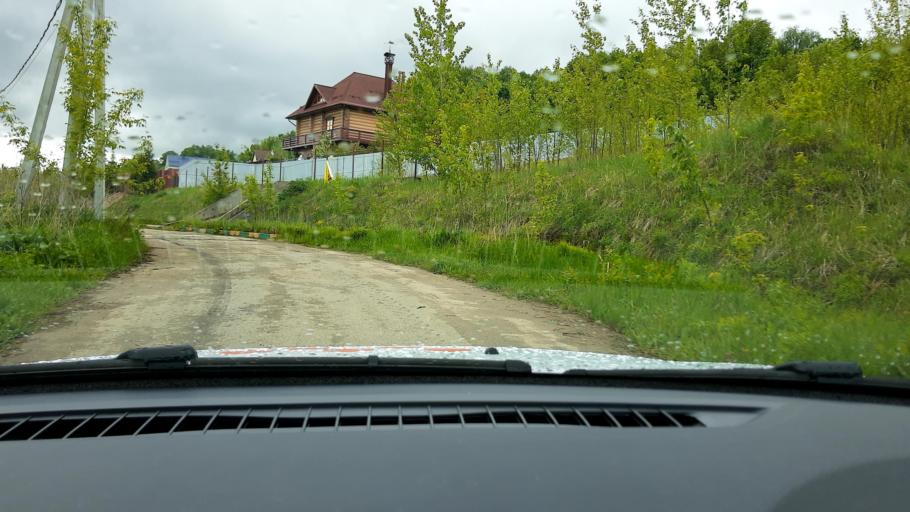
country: RU
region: Nizjnij Novgorod
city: Afonino
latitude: 56.2682
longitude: 44.0985
